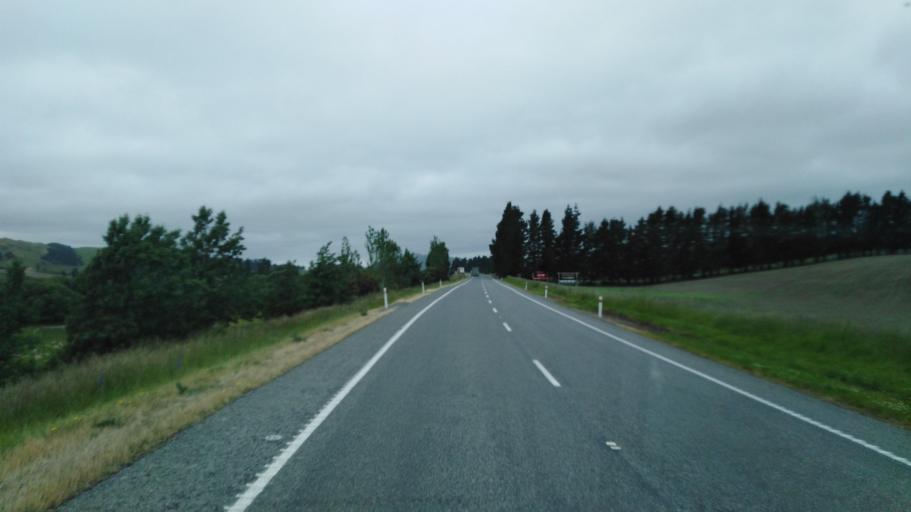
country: NZ
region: Canterbury
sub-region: Hurunui District
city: Amberley
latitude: -42.9569
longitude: 172.9995
